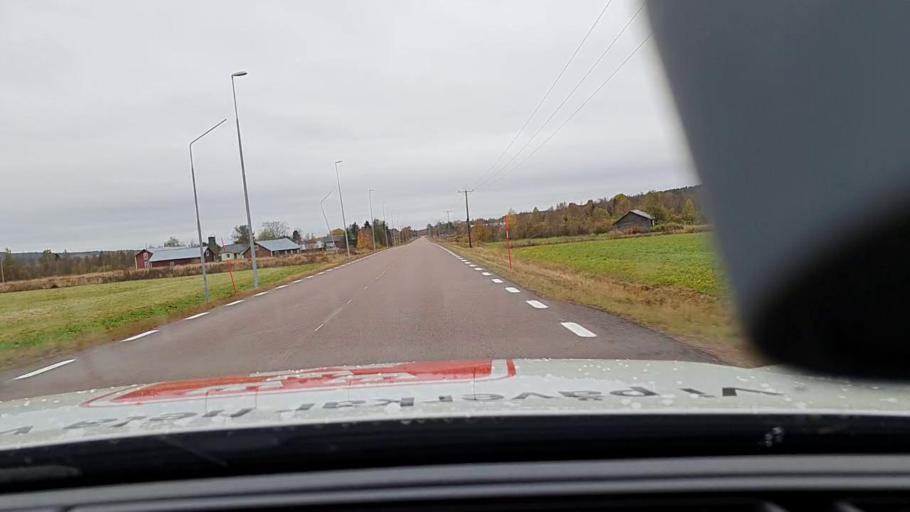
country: FI
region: Lapland
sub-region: Torniolaakso
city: Ylitornio
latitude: 66.1400
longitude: 23.9002
